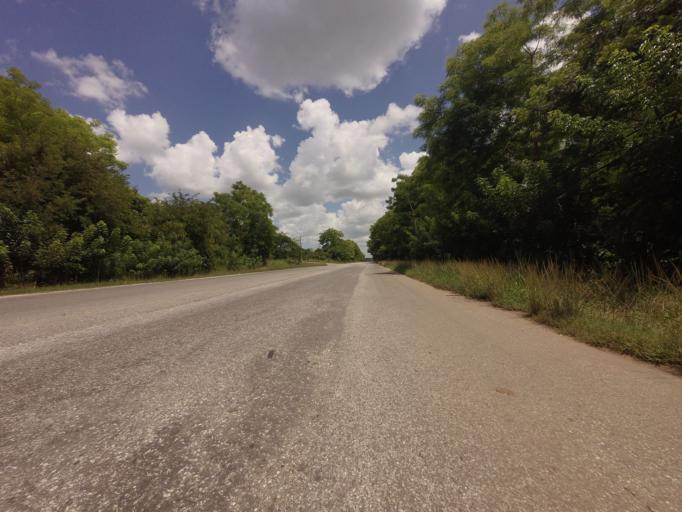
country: CU
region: La Habana
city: Arroyo Naranjo
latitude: 23.0373
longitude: -82.3382
